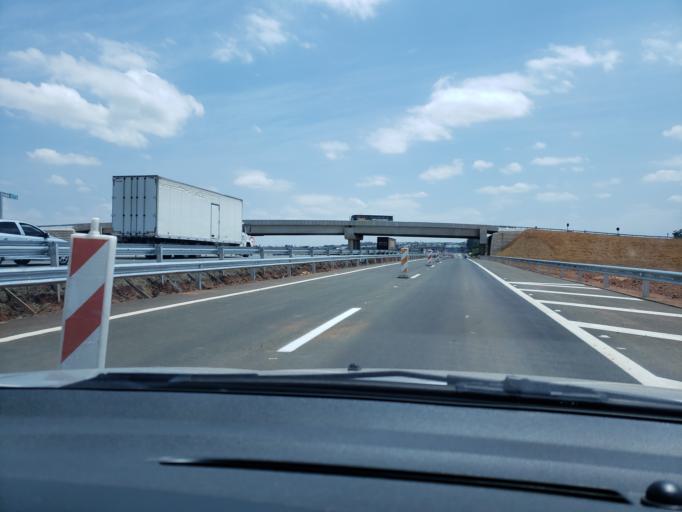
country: BR
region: Sao Paulo
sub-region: Campinas
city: Campinas
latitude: -22.8518
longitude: -47.1160
